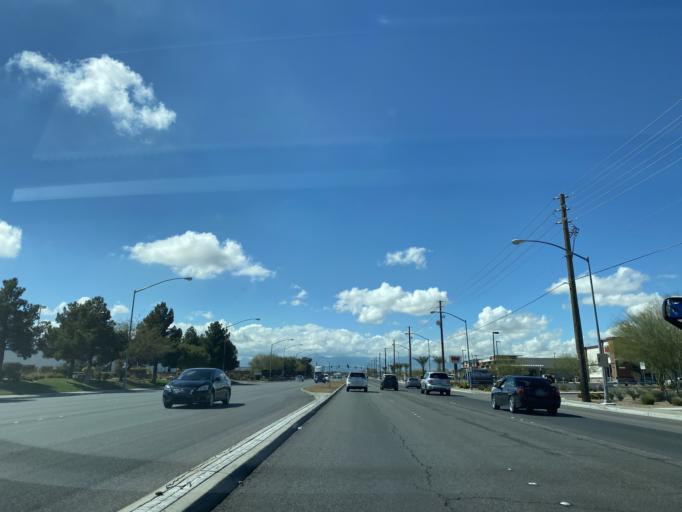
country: US
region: Nevada
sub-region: Clark County
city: North Las Vegas
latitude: 36.2398
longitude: -115.1215
